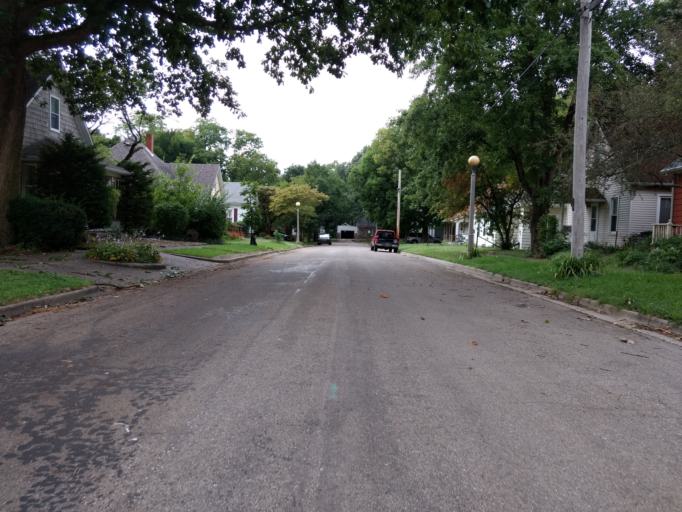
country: US
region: Illinois
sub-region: Champaign County
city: Urbana
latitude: 40.1140
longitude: -88.1965
